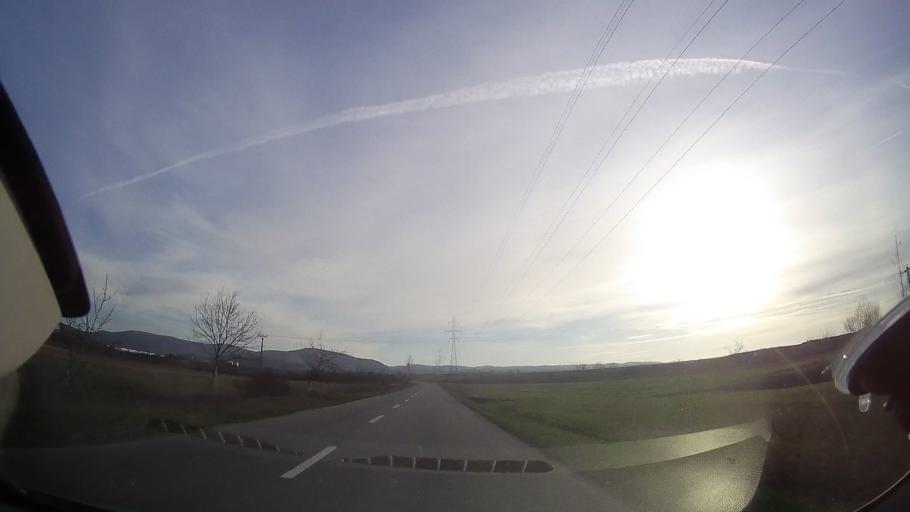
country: RO
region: Bihor
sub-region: Comuna Tetchea
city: Hotar
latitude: 47.0502
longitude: 22.3086
